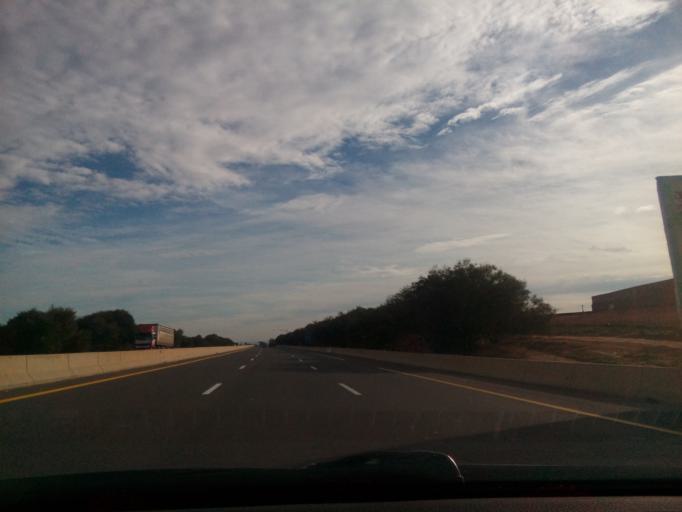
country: DZ
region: Mascara
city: Sig
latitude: 35.5419
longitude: -0.3642
